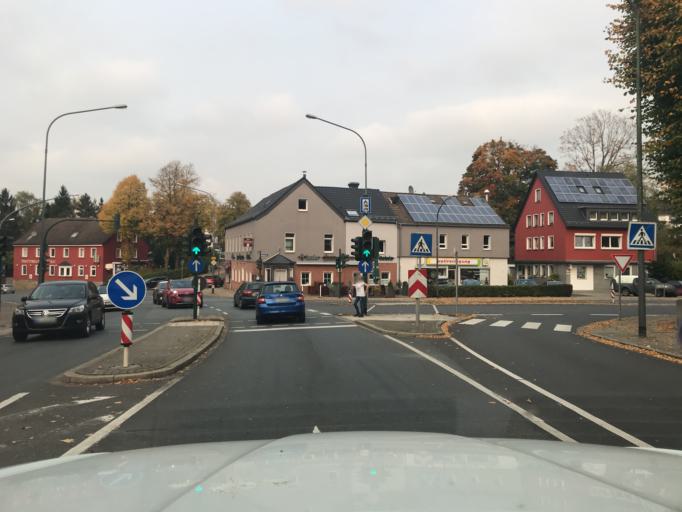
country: DE
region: North Rhine-Westphalia
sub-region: Regierungsbezirk Dusseldorf
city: Velbert
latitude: 51.3853
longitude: 7.0257
